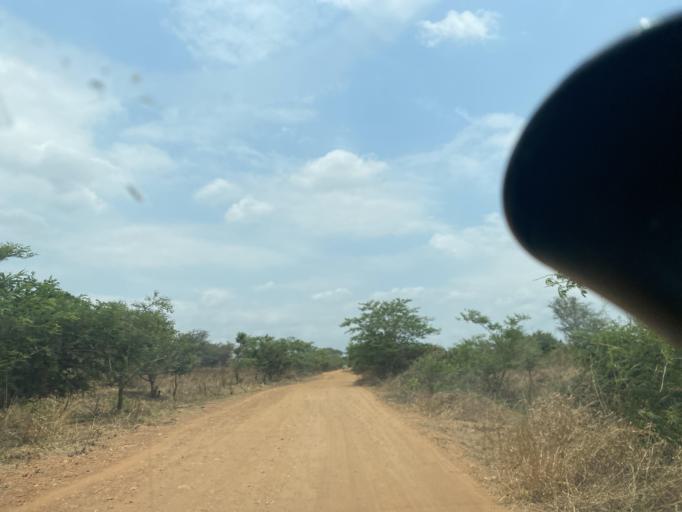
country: ZM
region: Lusaka
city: Chongwe
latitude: -15.5206
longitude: 28.8219
